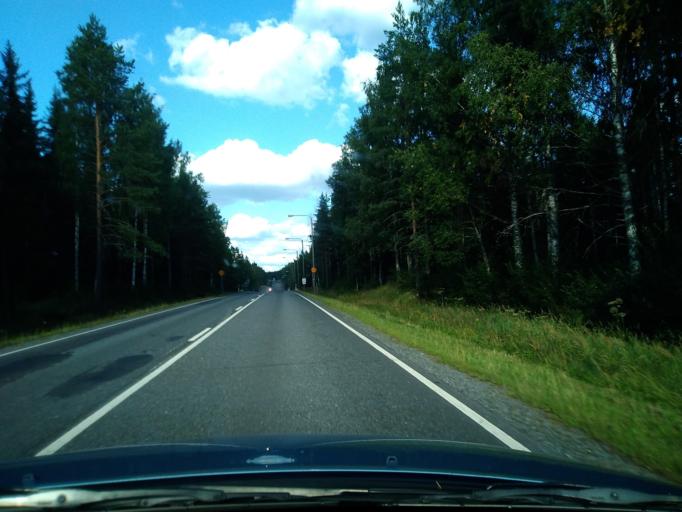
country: FI
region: Pirkanmaa
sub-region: Ylae-Pirkanmaa
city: Maenttae
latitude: 62.0183
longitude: 24.6828
